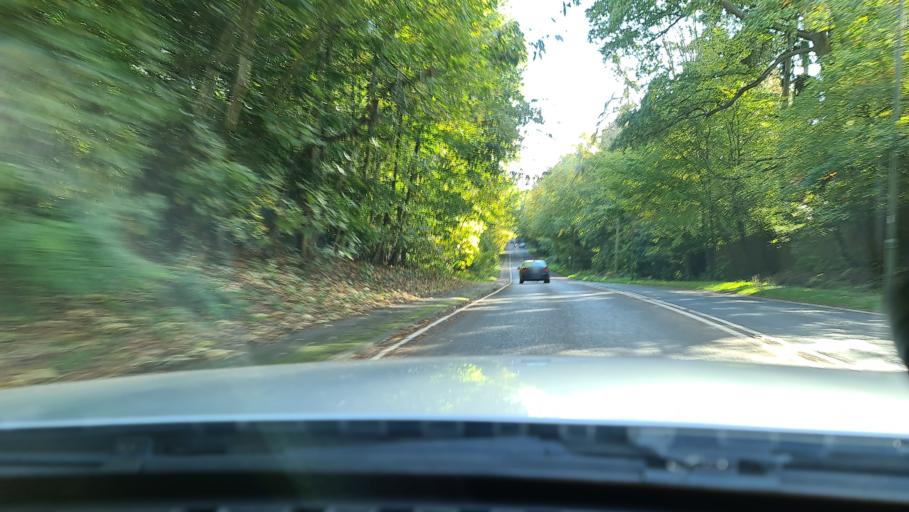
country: GB
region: England
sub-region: Surrey
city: Weybridge
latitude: 51.3499
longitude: -0.4351
